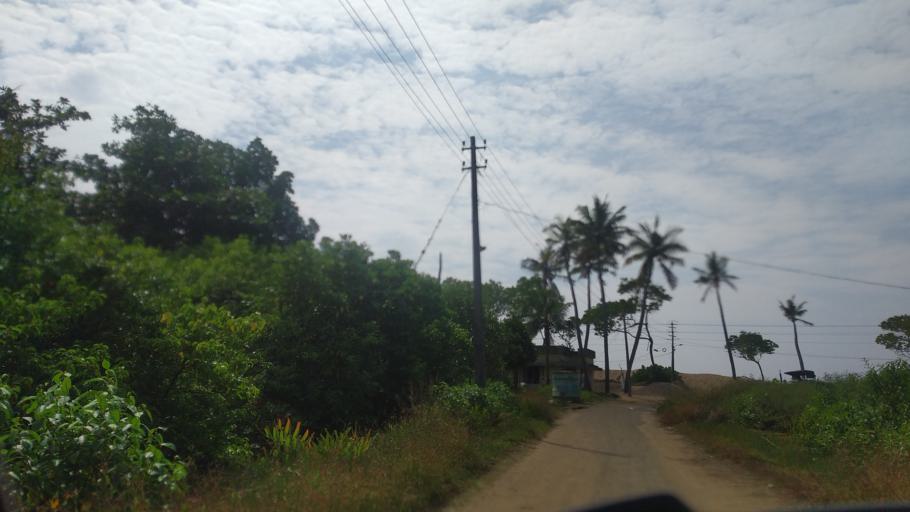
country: IN
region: Kerala
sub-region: Ernakulam
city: Elur
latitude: 10.0813
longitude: 76.1954
